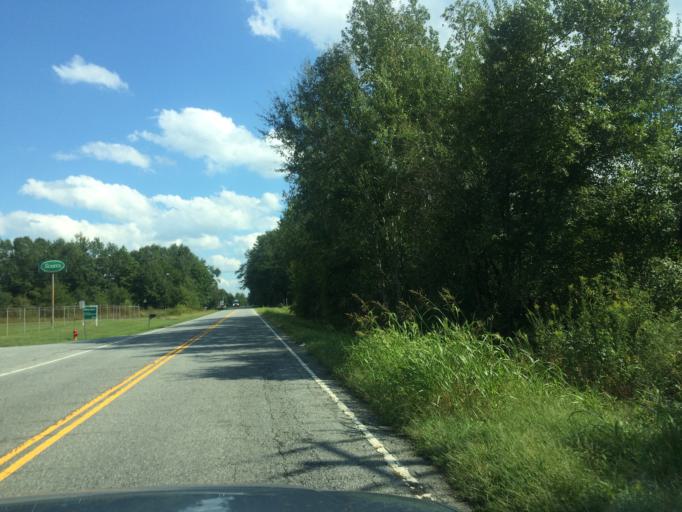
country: US
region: South Carolina
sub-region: Anderson County
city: Honea Path
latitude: 34.4721
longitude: -82.4303
